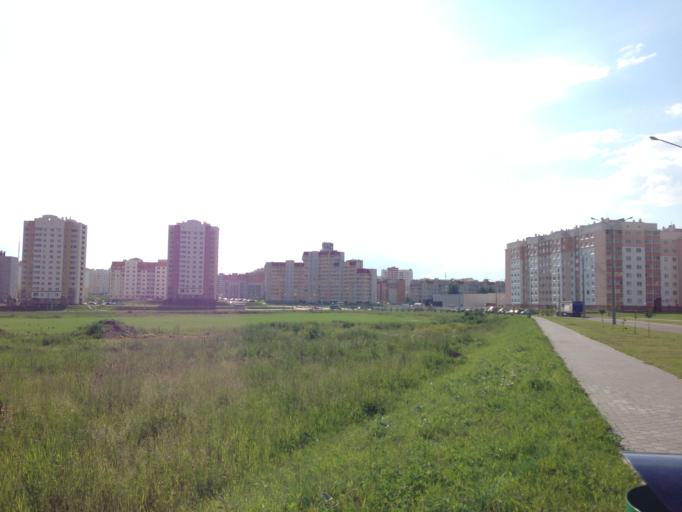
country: BY
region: Grodnenskaya
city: Hrodna
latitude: 53.7102
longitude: 23.8651
